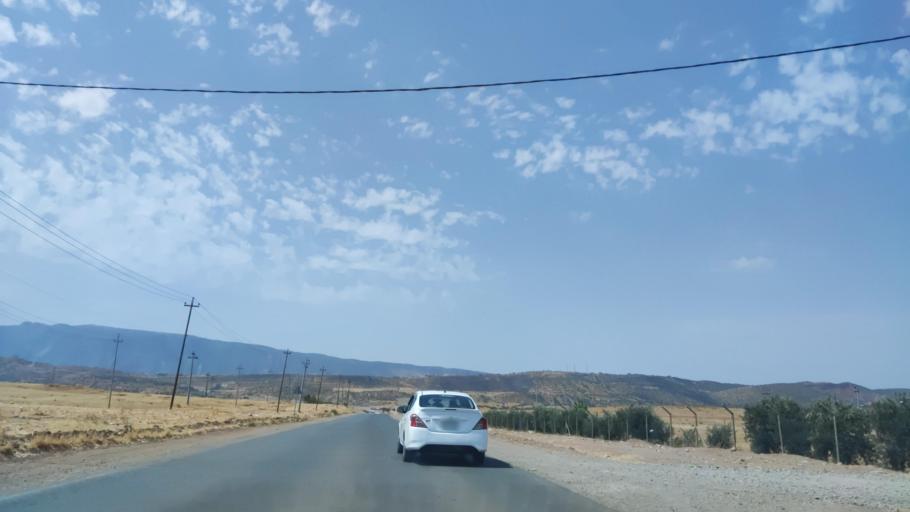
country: IQ
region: Arbil
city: Shaqlawah
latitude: 36.4620
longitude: 44.3905
